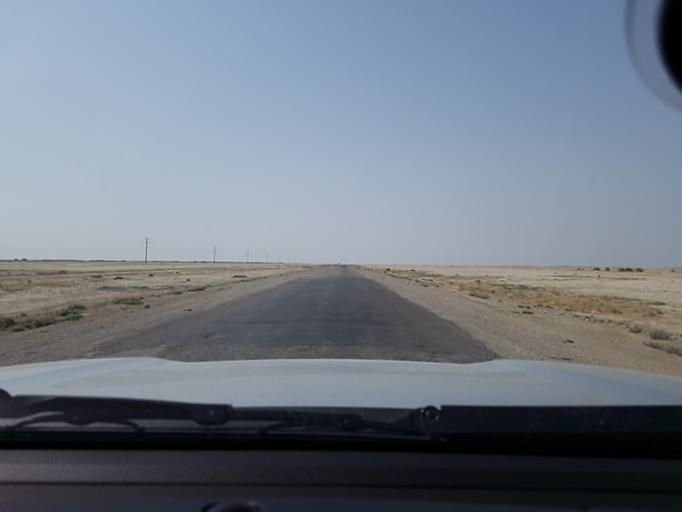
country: TM
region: Balkan
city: Gumdag
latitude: 38.8491
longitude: 54.5954
